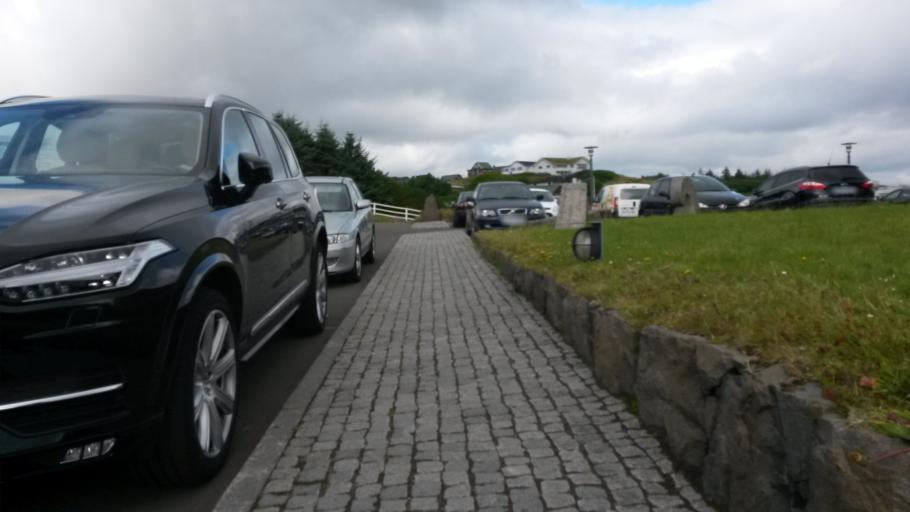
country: FO
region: Streymoy
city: Hoyvik
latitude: 62.0221
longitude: -6.7853
